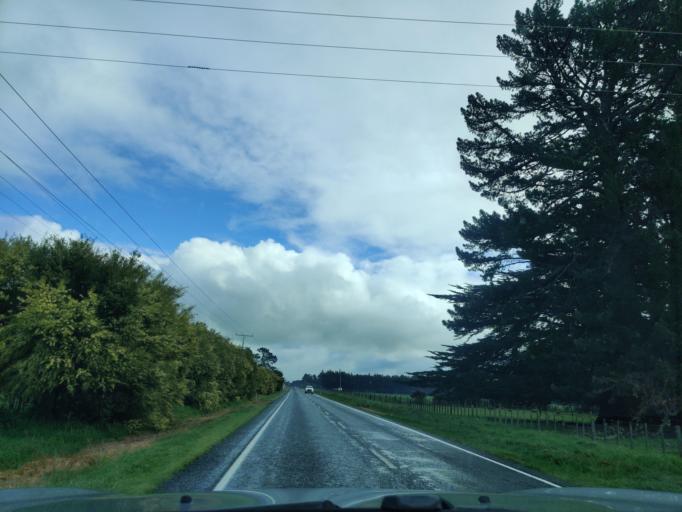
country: NZ
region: Hawke's Bay
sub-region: Hastings District
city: Hastings
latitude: -40.0183
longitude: 176.3476
